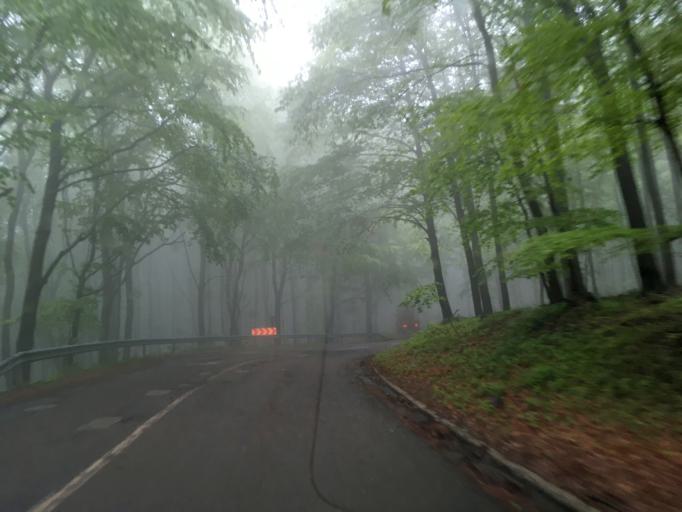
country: HU
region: Heves
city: Paradsasvar
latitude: 47.8697
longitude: 20.0023
